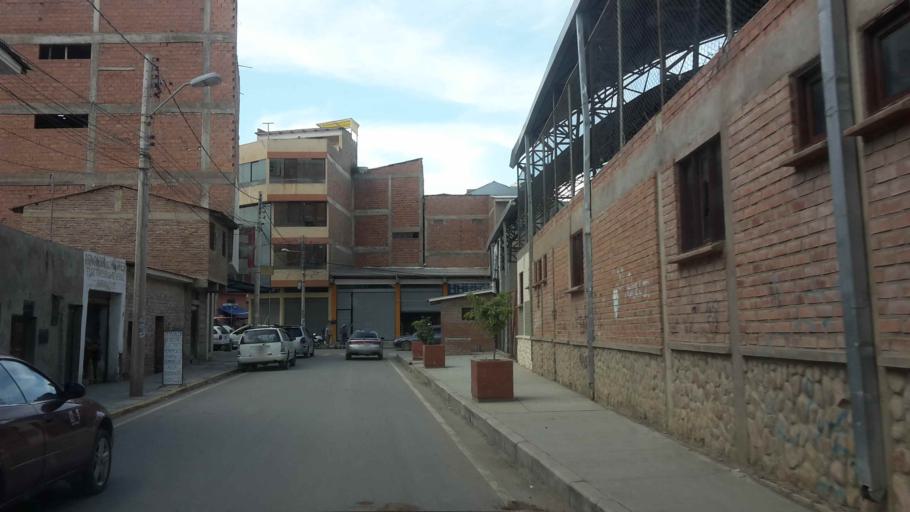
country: BO
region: Cochabamba
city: Sipe Sipe
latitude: -17.4015
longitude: -66.2822
